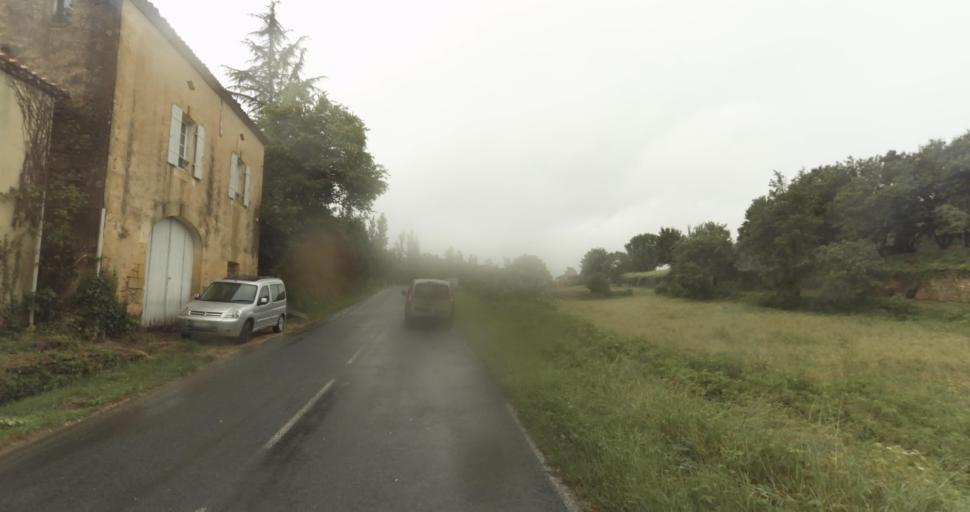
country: FR
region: Aquitaine
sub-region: Departement de la Dordogne
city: Beaumont-du-Perigord
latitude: 44.7748
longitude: 0.8136
